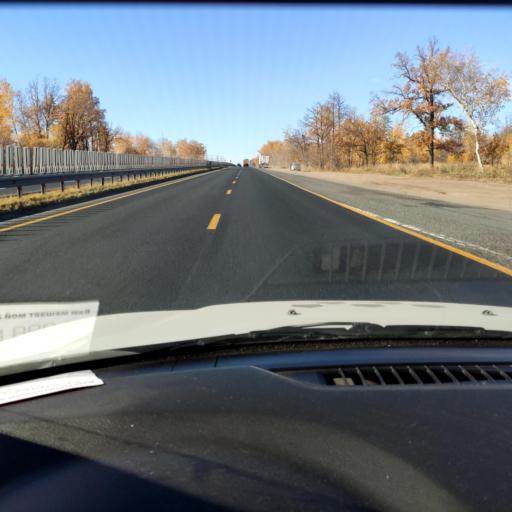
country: RU
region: Samara
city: Pribrezhnyy
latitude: 53.5121
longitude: 49.9255
